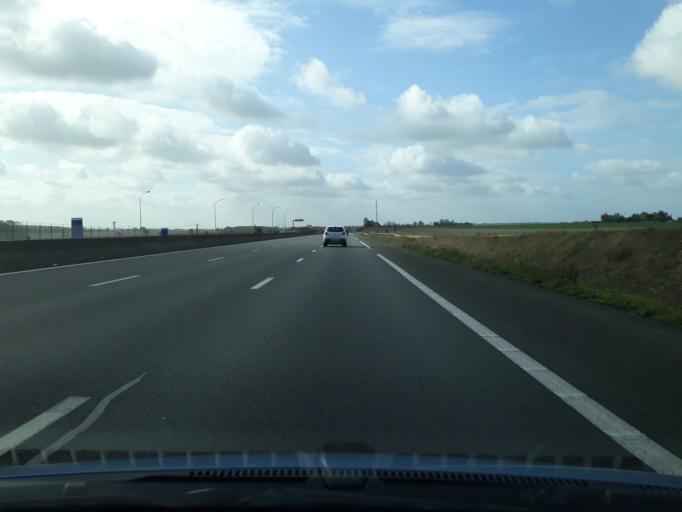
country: FR
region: Centre
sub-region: Departement du Loir-et-Cher
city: La Chaussee-Saint-Victor
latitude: 47.6637
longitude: 1.3865
